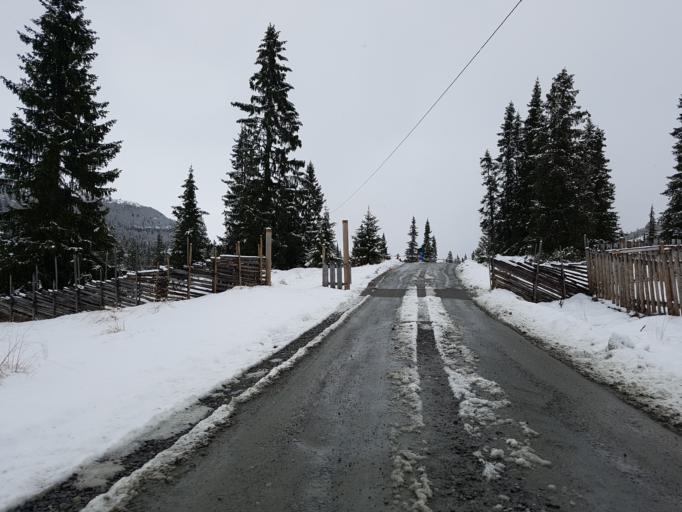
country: NO
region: Oppland
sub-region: Sel
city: Otta
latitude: 61.8072
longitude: 9.6852
